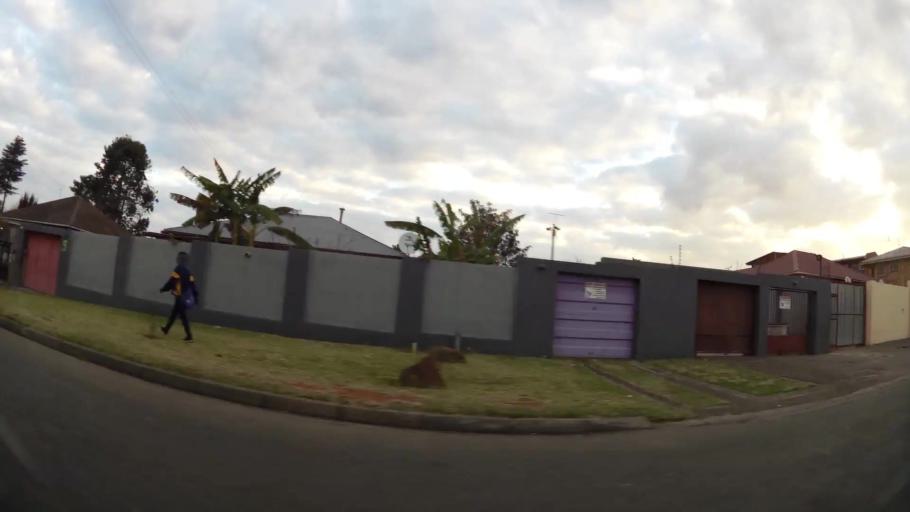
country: ZA
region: Gauteng
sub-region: Ekurhuleni Metropolitan Municipality
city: Germiston
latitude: -26.1943
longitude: 28.1529
